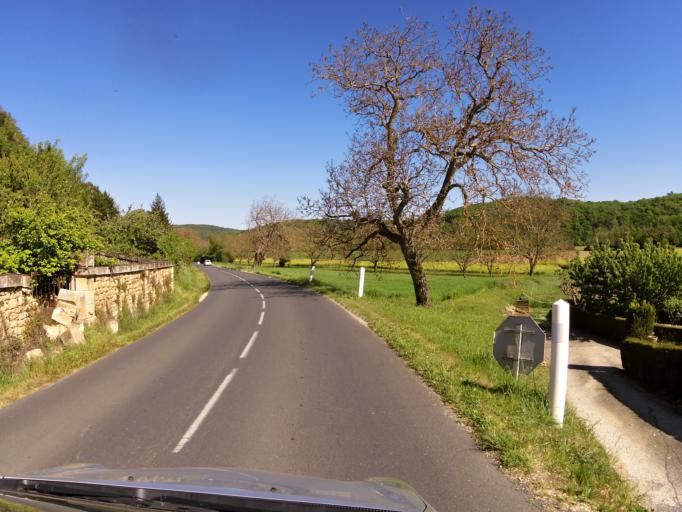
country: FR
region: Aquitaine
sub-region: Departement de la Dordogne
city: Cenac-et-Saint-Julien
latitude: 44.8218
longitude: 1.1597
